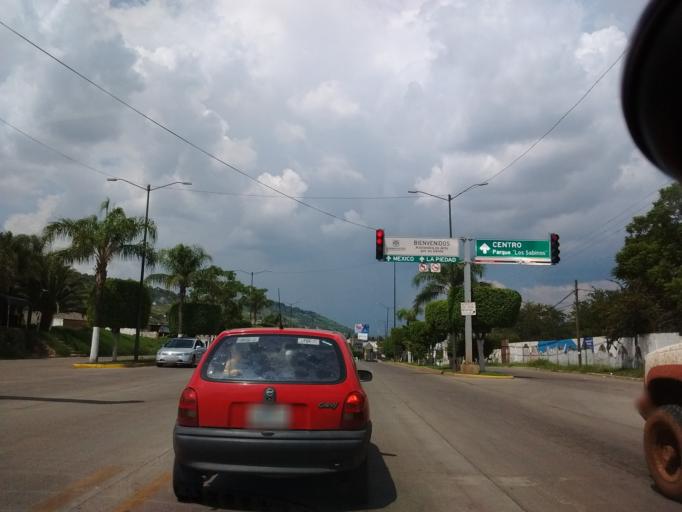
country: MX
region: Jalisco
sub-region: Atotonilco el Alto
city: Vistas del Maguey [Fraccionamiento]
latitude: 20.5387
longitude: -102.5165
